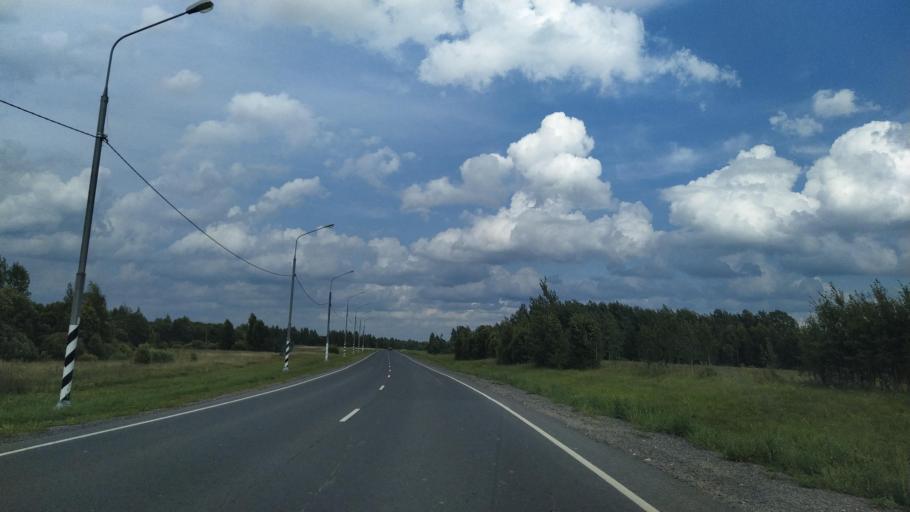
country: RU
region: Pskov
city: Dno
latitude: 58.0632
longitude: 30.0292
